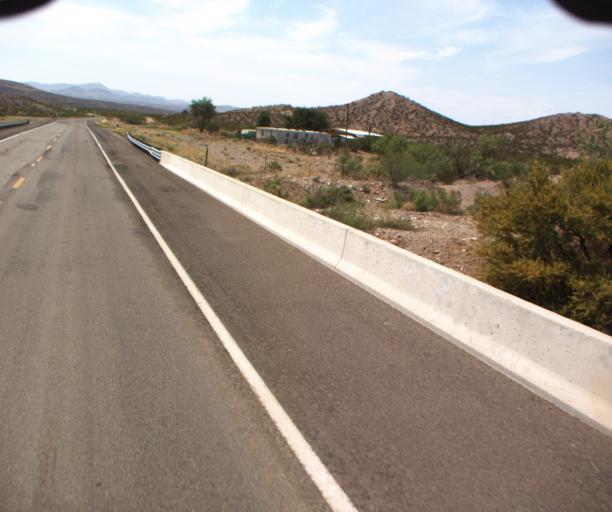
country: US
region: Arizona
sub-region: Greenlee County
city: Clifton
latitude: 32.7652
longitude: -109.1459
